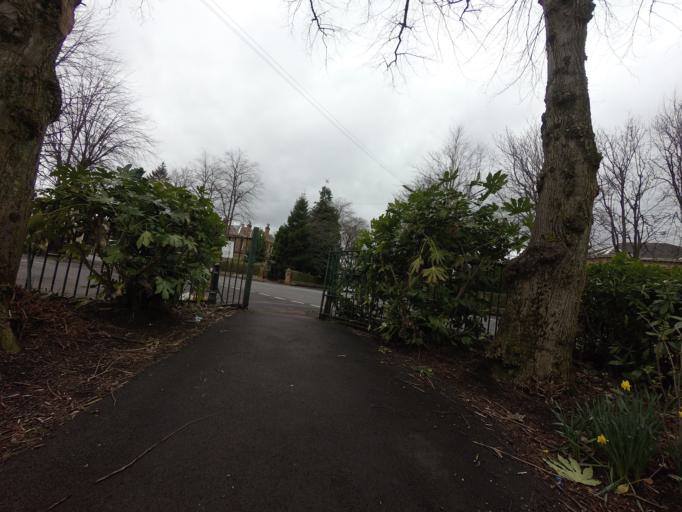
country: GB
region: Scotland
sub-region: East Renfrewshire
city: Giffnock
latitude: 55.8385
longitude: -4.2927
